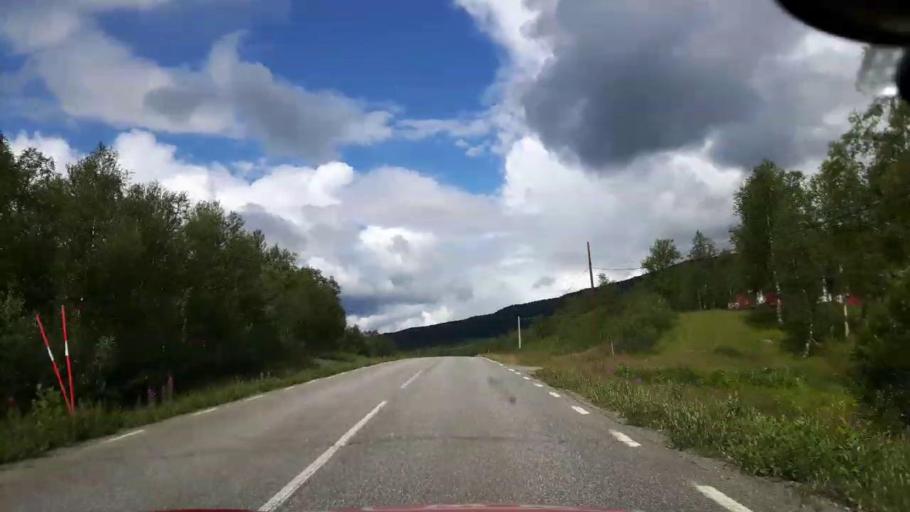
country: NO
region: Nordland
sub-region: Hattfjelldal
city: Hattfjelldal
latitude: 65.0572
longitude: 14.7225
